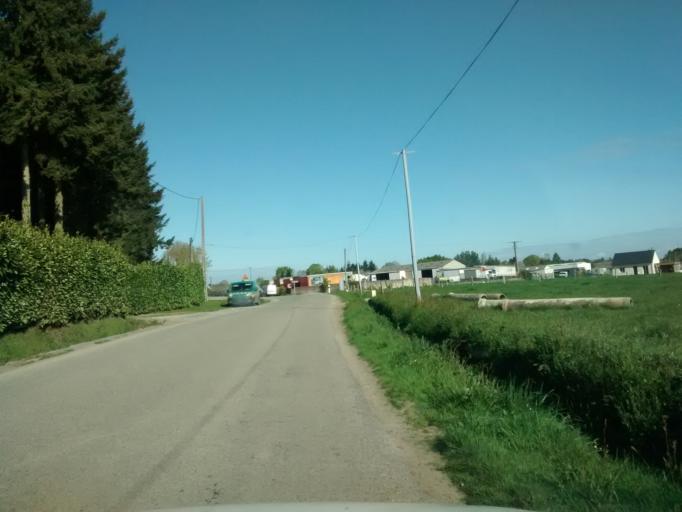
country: FR
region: Brittany
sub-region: Departement du Morbihan
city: Malestroit
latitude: 47.8620
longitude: -2.4146
